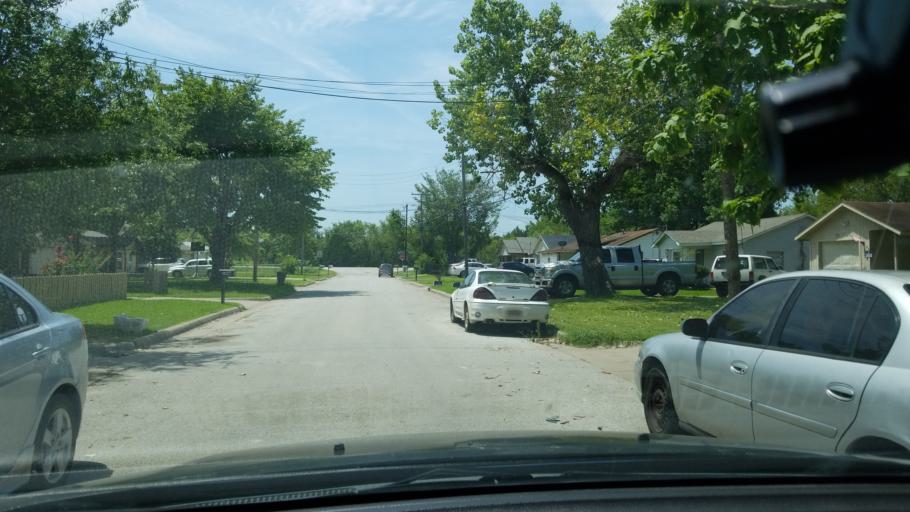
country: US
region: Texas
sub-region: Dallas County
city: Balch Springs
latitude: 32.7497
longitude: -96.6281
